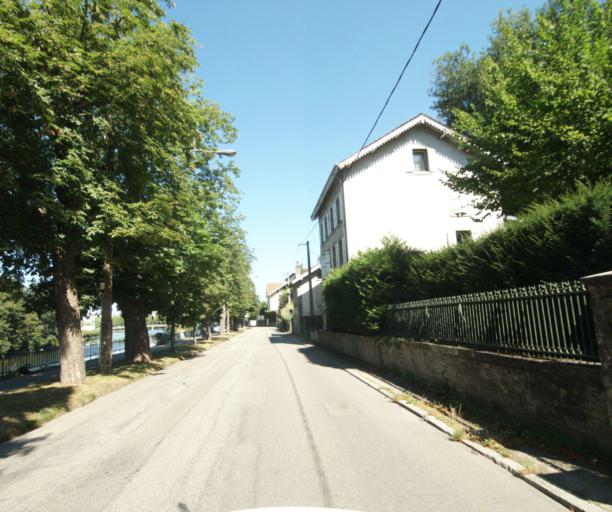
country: FR
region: Lorraine
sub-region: Departement des Vosges
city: Epinal
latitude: 48.1630
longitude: 6.4560
